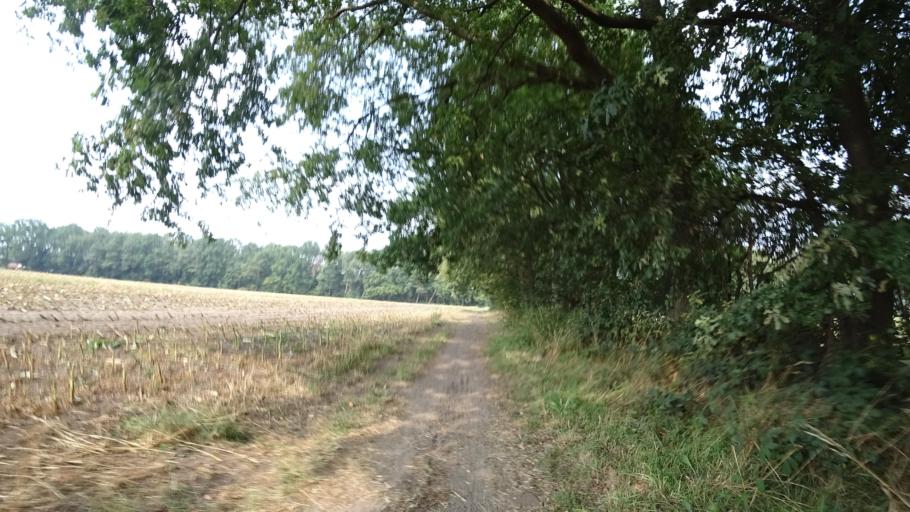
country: DE
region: North Rhine-Westphalia
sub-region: Regierungsbezirk Detmold
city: Guetersloh
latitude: 51.9201
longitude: 8.4380
